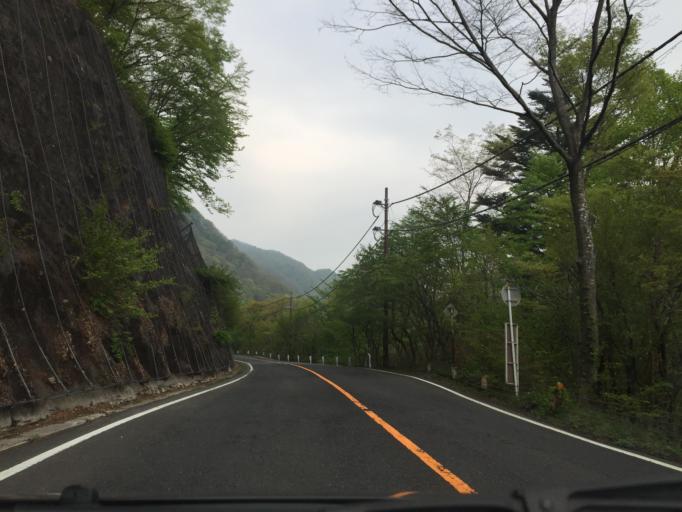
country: JP
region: Tochigi
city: Nikko
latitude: 36.8982
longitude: 139.7082
